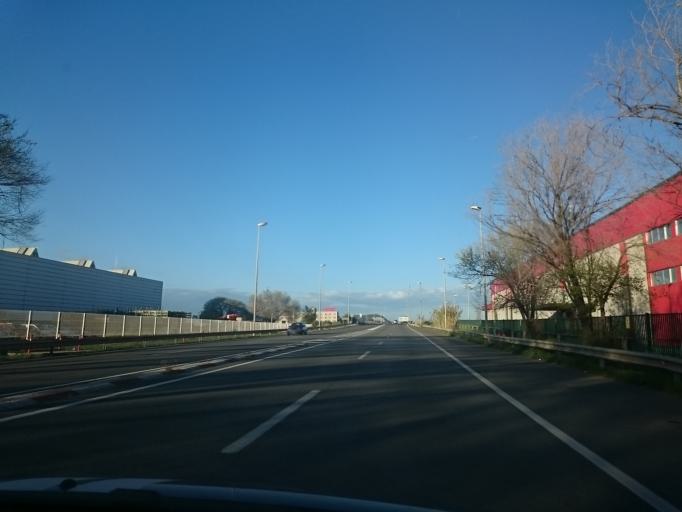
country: ES
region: Catalonia
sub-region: Provincia de Barcelona
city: El Prat de Llobregat
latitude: 41.3252
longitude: 2.1093
